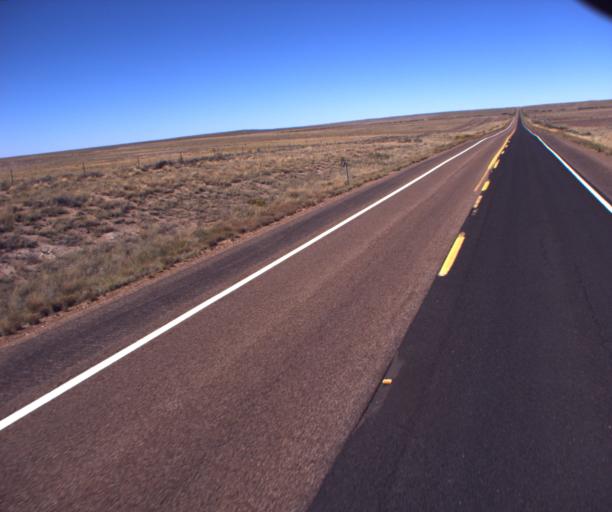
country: US
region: Arizona
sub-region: Navajo County
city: Snowflake
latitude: 34.7284
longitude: -109.7801
